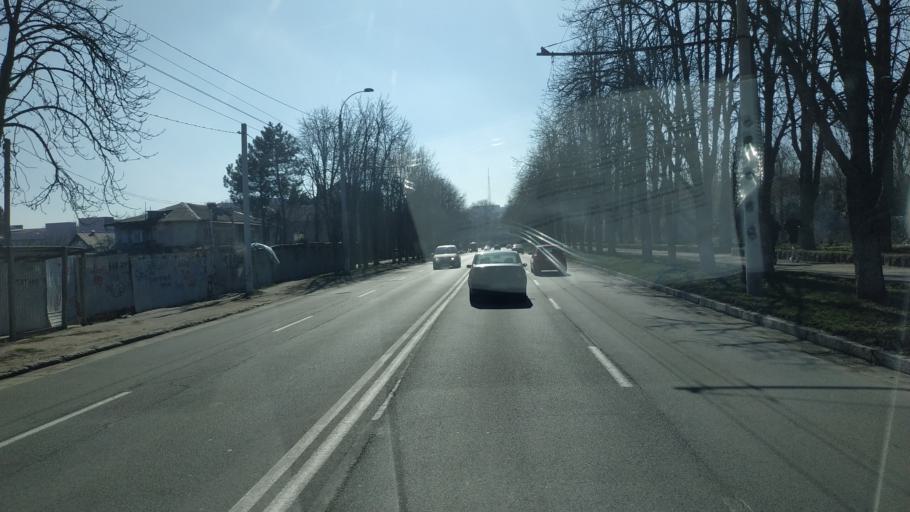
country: MD
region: Chisinau
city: Chisinau
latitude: 47.0241
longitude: 28.8033
